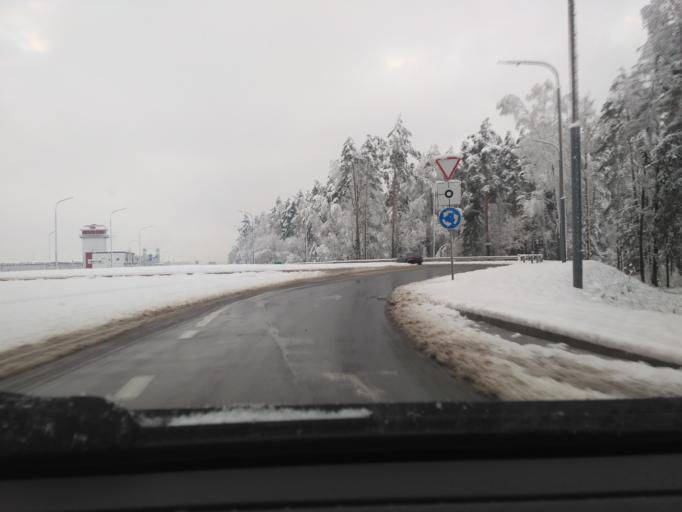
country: BY
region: Minsk
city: Horad Zhodzina
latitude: 54.1406
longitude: 28.3856
